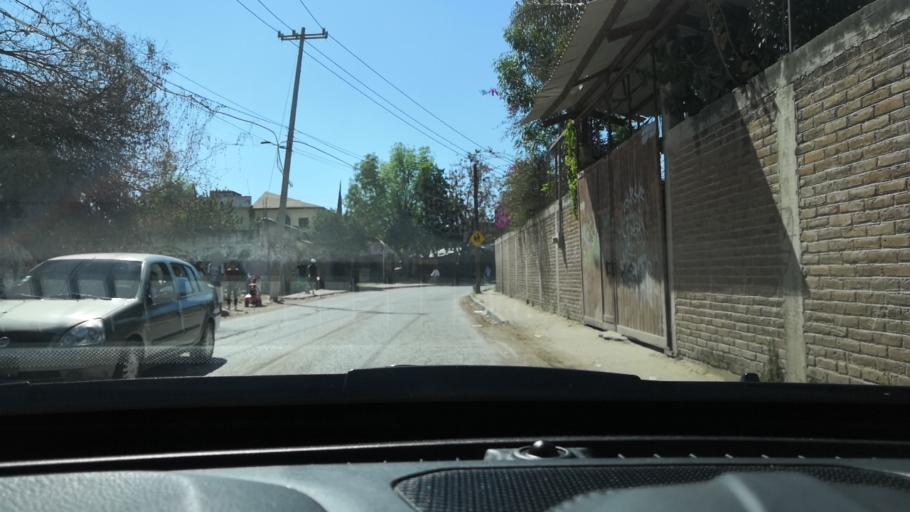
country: MX
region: Guanajuato
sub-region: Leon
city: Centro Familiar la Soledad
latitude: 21.1338
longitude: -101.7450
